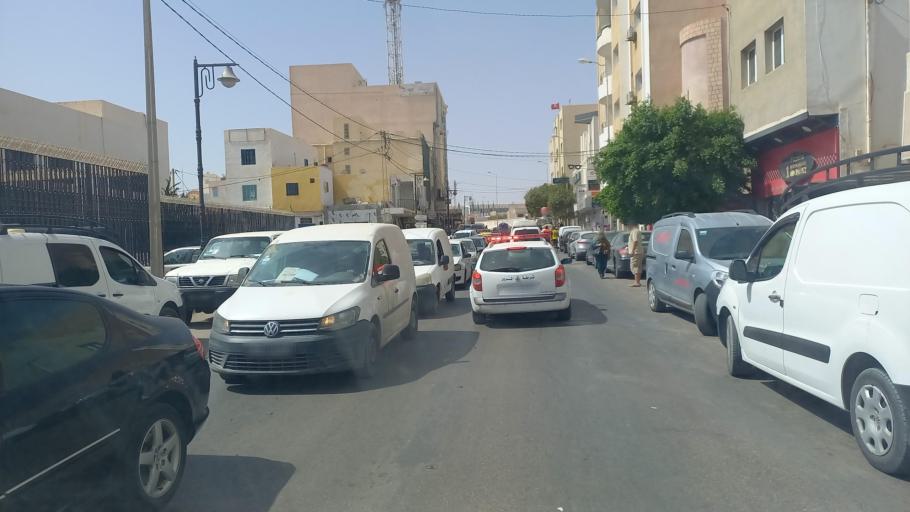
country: TN
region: Madanin
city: Medenine
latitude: 33.3423
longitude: 10.4893
